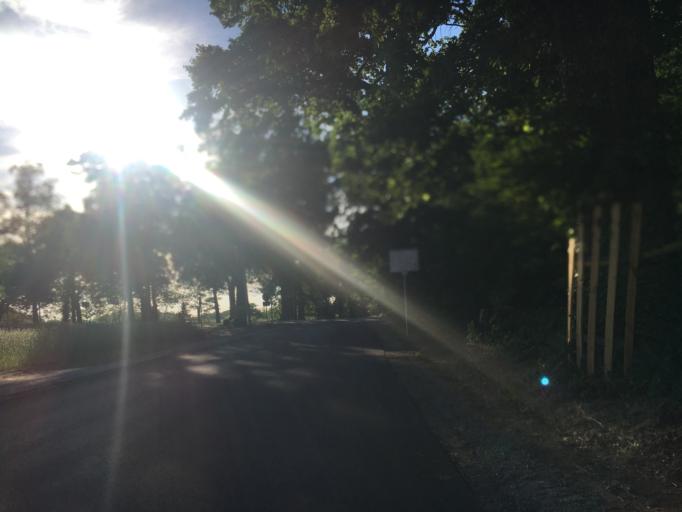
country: DE
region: Brandenburg
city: Potsdam
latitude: 52.4323
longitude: 13.0443
